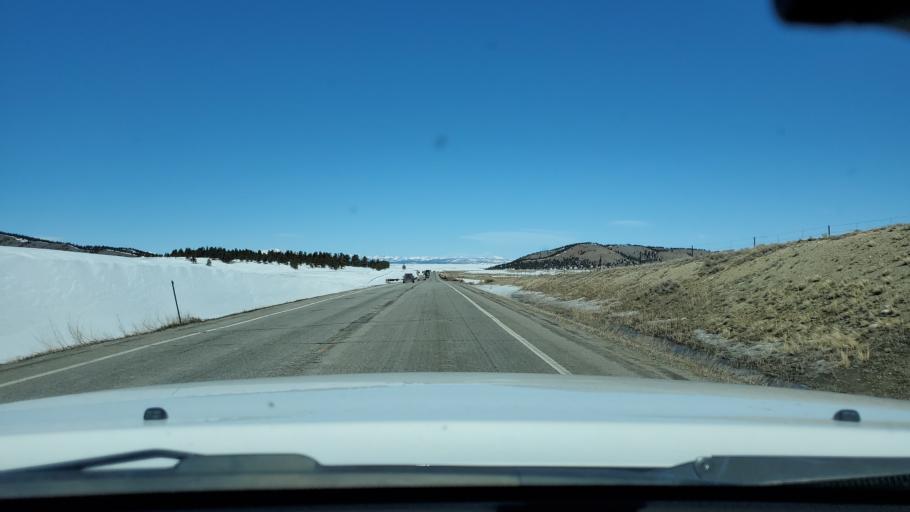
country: US
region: Colorado
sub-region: Chaffee County
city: Buena Vista
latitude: 38.9349
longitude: -105.9640
